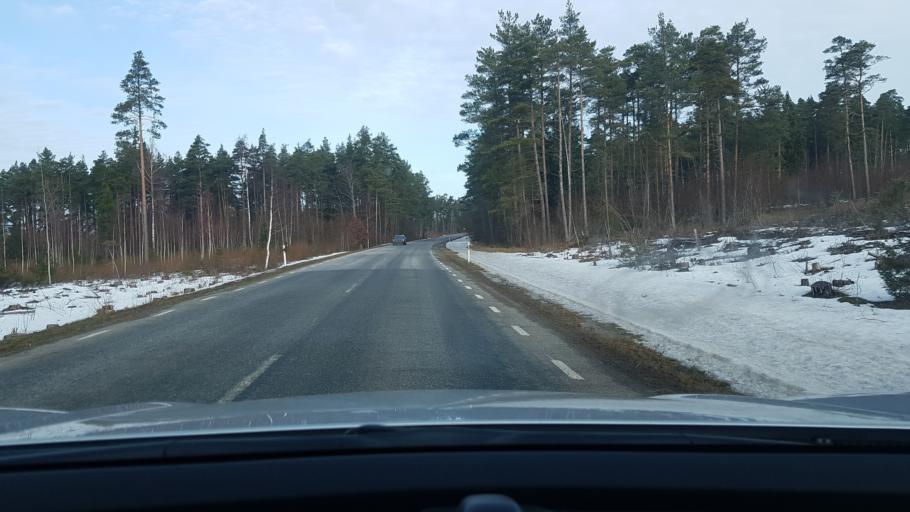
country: EE
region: Saare
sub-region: Kuressaare linn
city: Kuressaare
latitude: 58.4375
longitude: 22.7048
